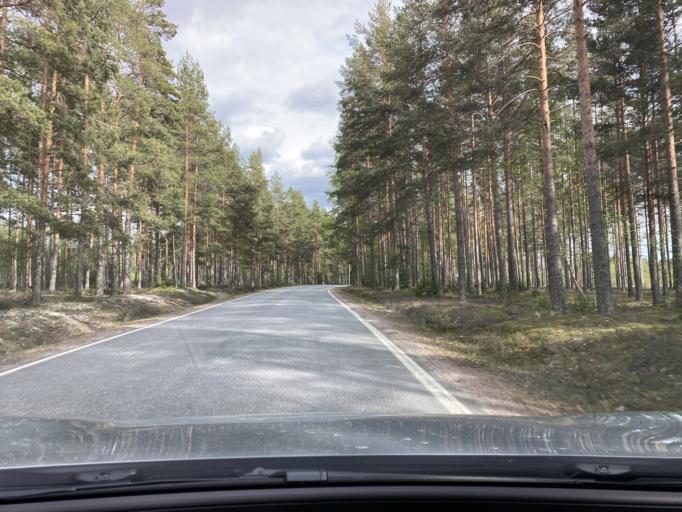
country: FI
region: Varsinais-Suomi
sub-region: Salo
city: Kiikala
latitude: 60.5111
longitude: 23.5362
